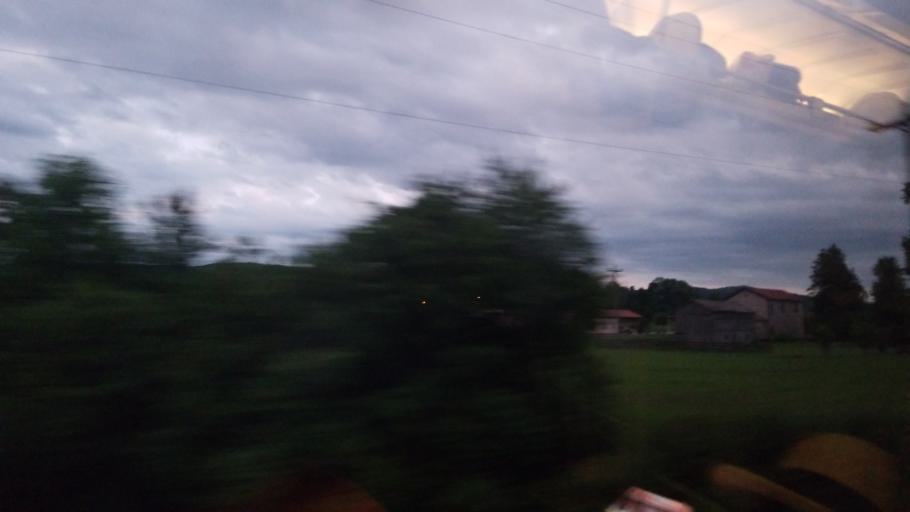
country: US
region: Virginia
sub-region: Orange County
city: Gordonsville
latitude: 38.1719
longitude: -78.2805
